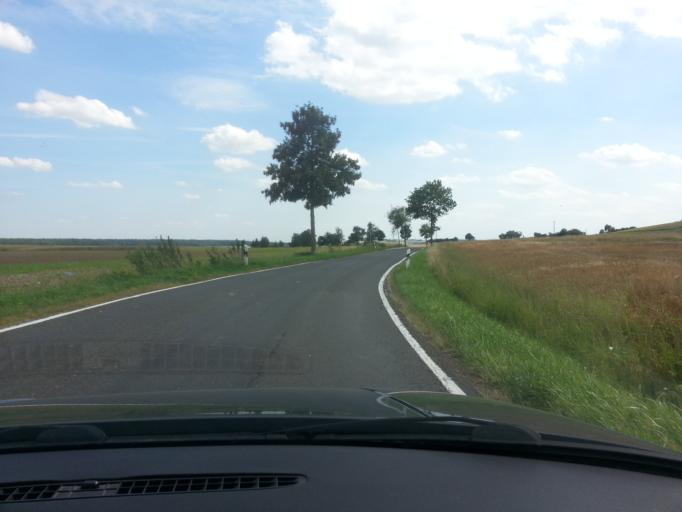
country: DE
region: Rheinland-Pfalz
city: Hornbach
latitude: 49.1792
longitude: 7.3005
